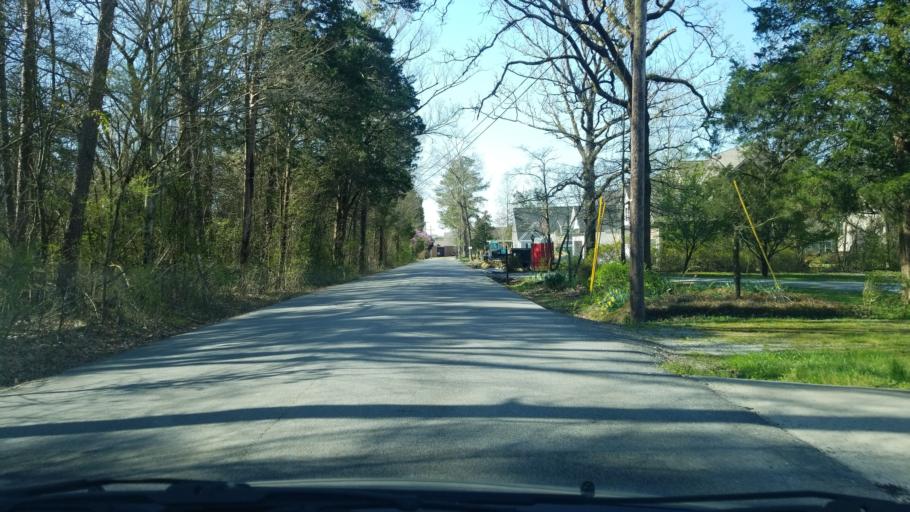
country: US
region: Tennessee
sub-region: Hamilton County
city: Harrison
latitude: 35.0610
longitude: -85.1454
